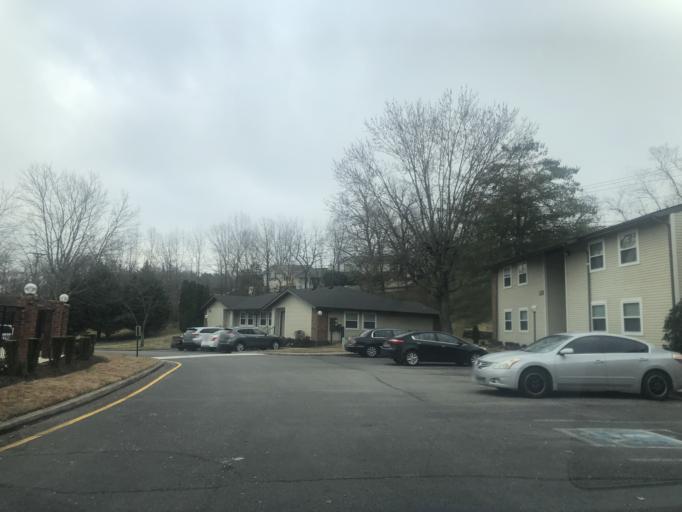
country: US
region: Tennessee
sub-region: Rutherford County
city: La Vergne
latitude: 36.0682
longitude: -86.6415
